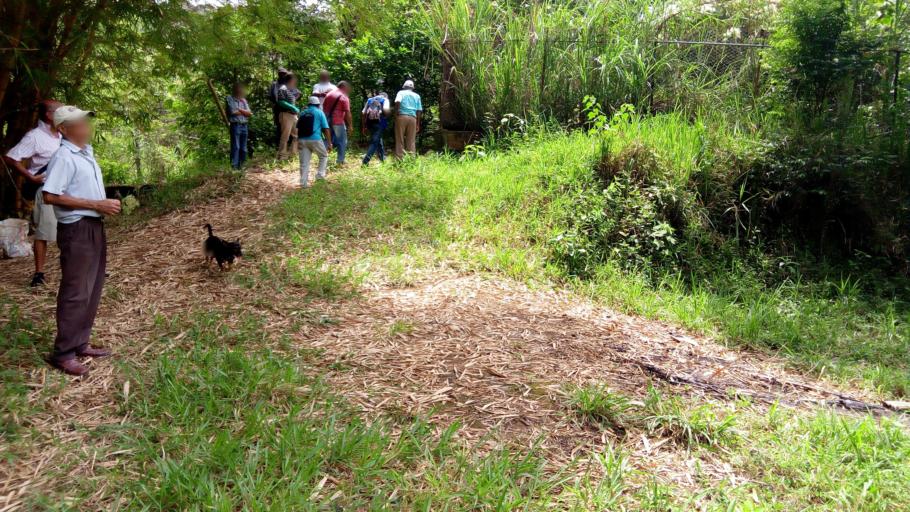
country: CO
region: Valle del Cauca
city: Cali
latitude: 3.3804
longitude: -76.5640
